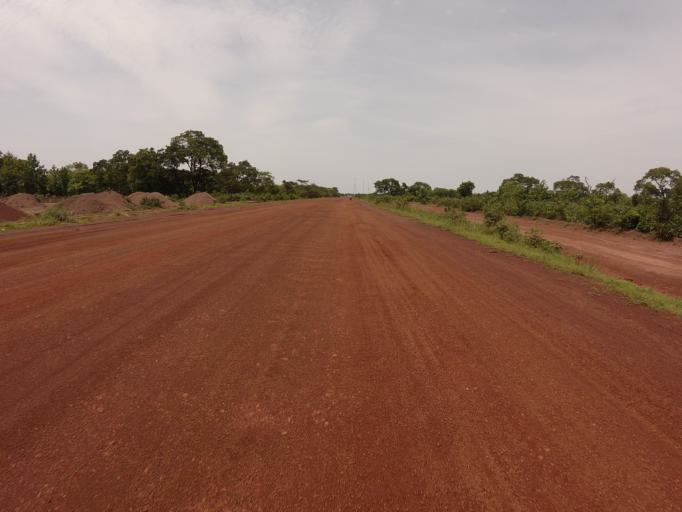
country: GH
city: Kpandae
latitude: 8.8818
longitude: 0.0334
